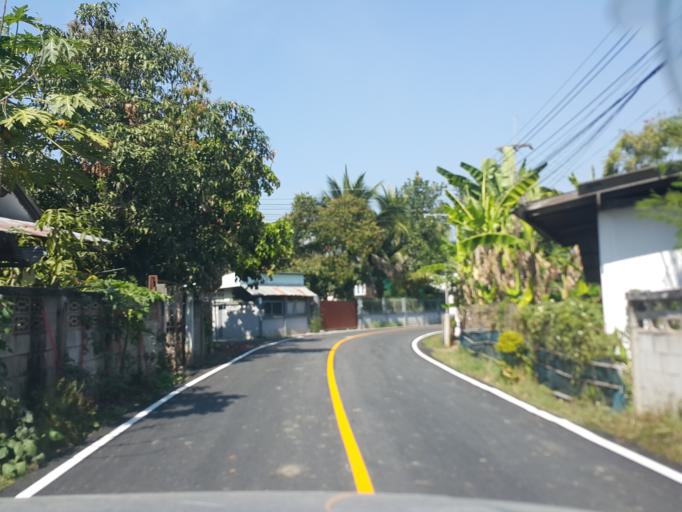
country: TH
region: Chiang Mai
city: San Kamphaeng
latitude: 18.8055
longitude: 99.1271
